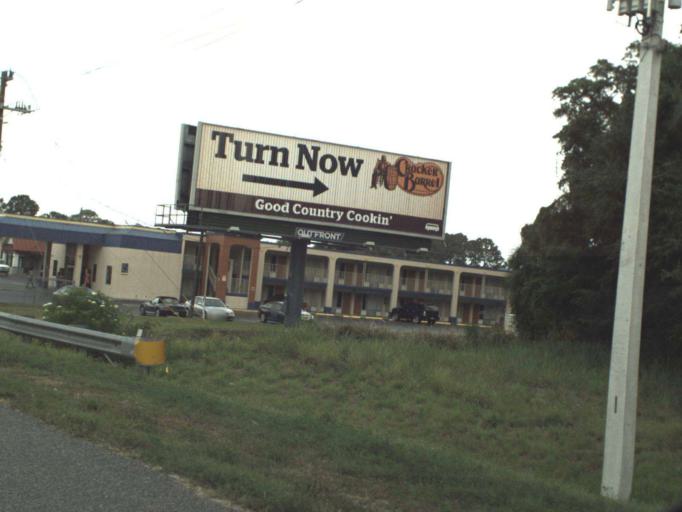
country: US
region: Florida
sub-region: Seminole County
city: Lake Mary
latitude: 28.8117
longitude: -81.3327
